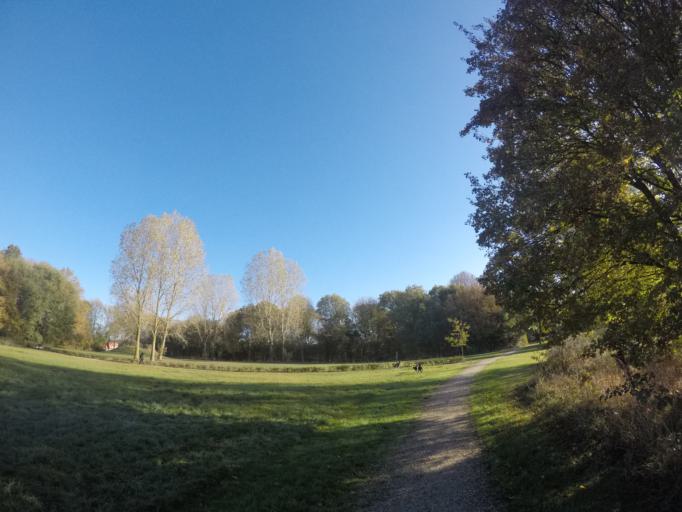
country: NL
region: Gelderland
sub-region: Gemeente Zevenaar
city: Zevenaar
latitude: 51.9184
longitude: 6.0731
